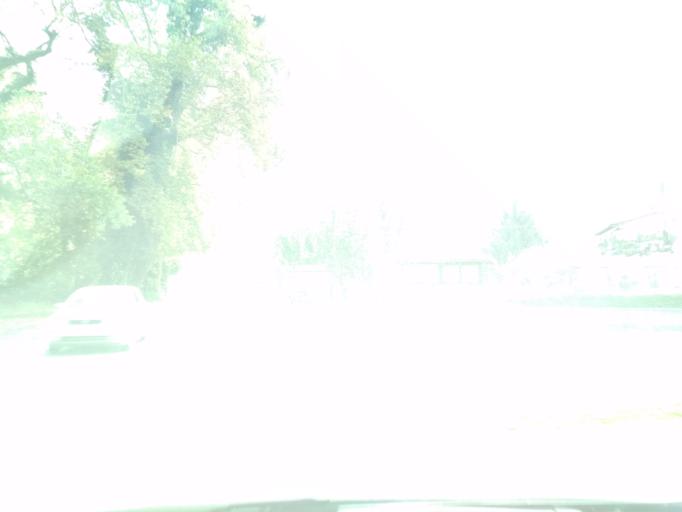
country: GR
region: Central Greece
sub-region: Nomos Evvoias
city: Prokopion
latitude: 38.7214
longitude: 23.5120
